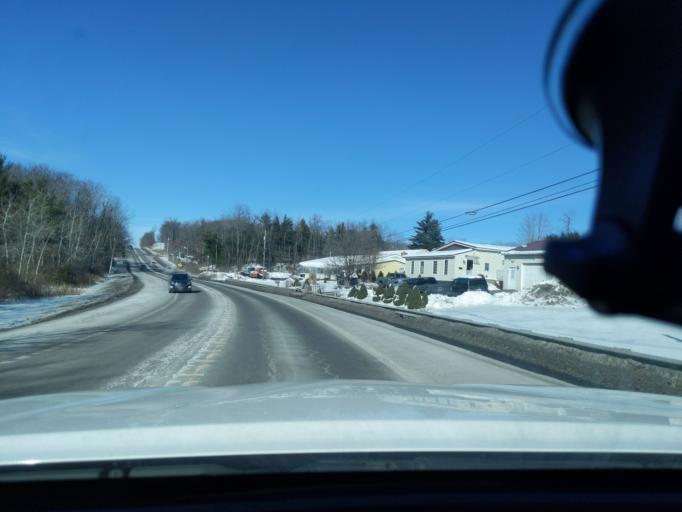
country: US
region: Maryland
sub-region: Allegany County
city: Frostburg
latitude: 39.6095
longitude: -78.9145
